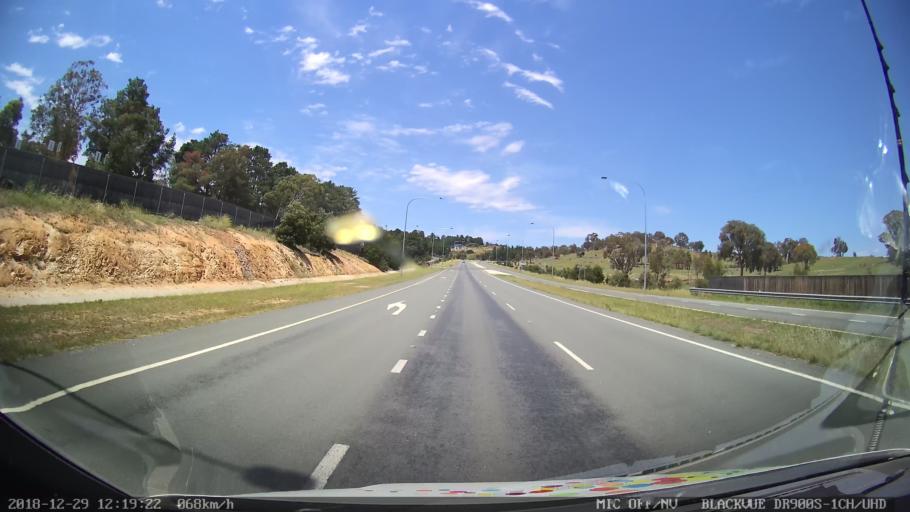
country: AU
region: New South Wales
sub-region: Queanbeyan
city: Queanbeyan
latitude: -35.3931
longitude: 149.2334
